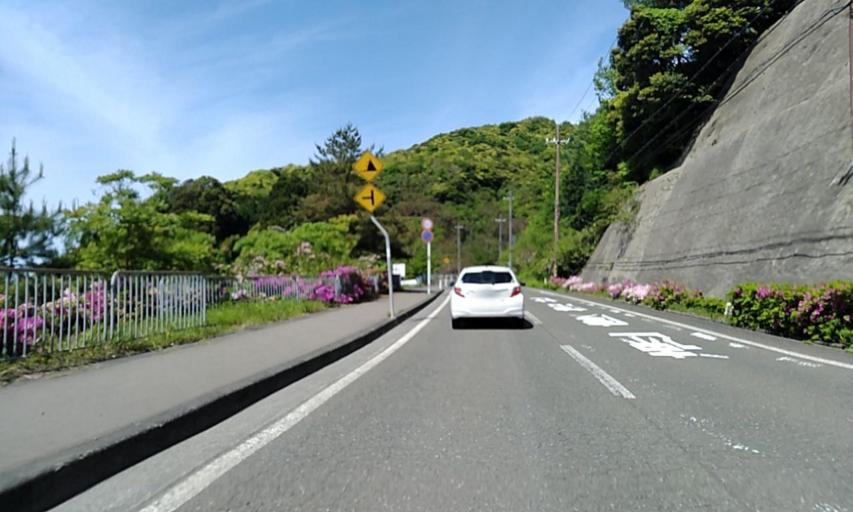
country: JP
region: Fukui
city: Obama
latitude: 35.5243
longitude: 135.8003
